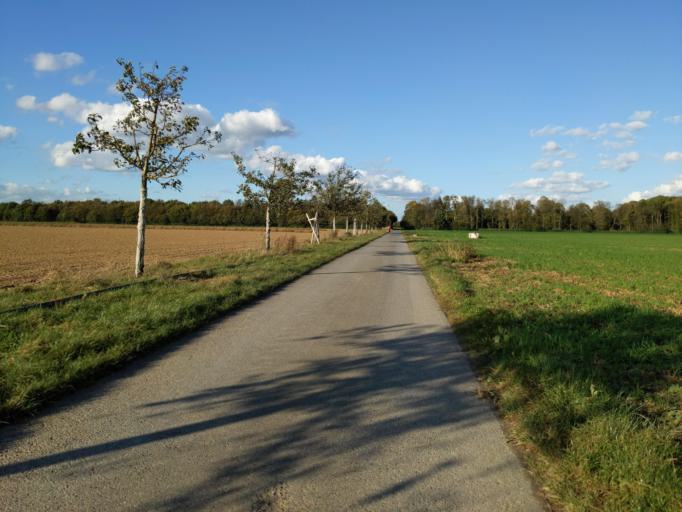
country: DE
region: North Rhine-Westphalia
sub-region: Regierungsbezirk Dusseldorf
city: Kaarst
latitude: 51.2076
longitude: 6.6013
